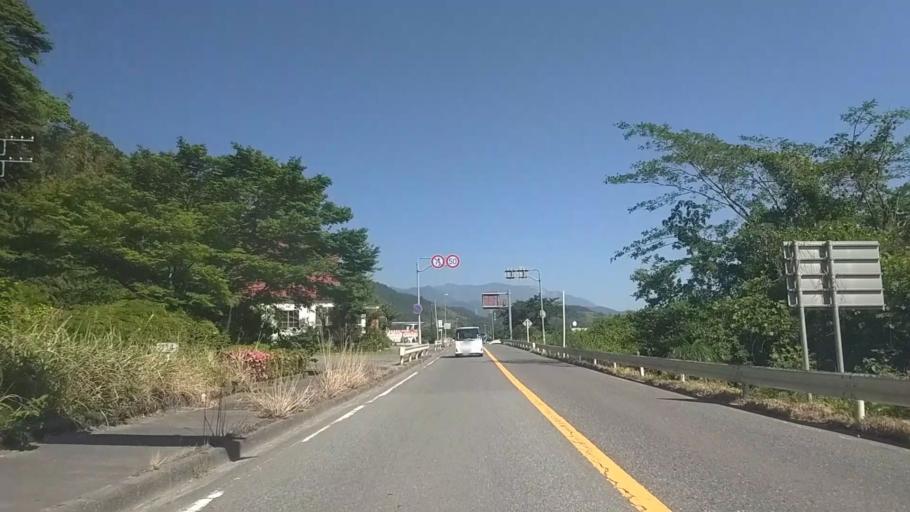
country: JP
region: Shizuoka
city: Fujinomiya
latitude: 35.2392
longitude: 138.4887
